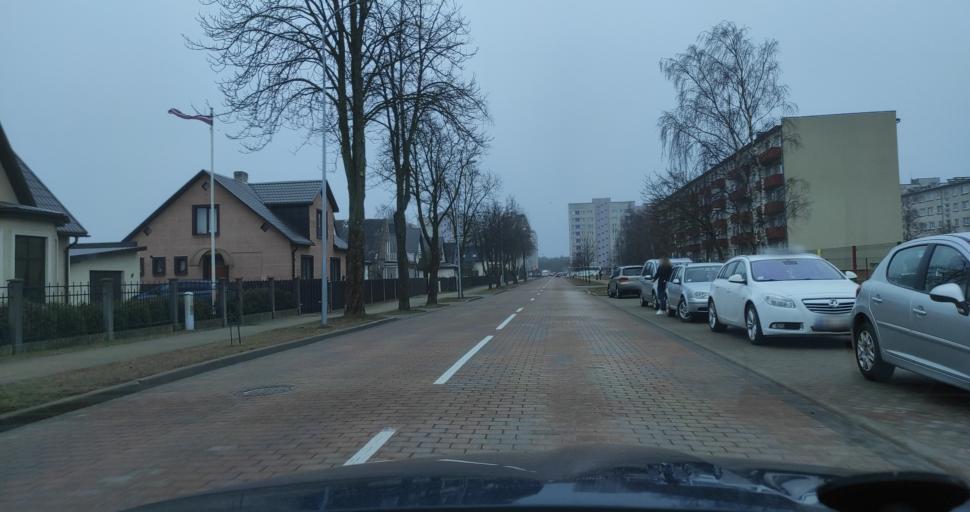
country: LV
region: Ventspils
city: Ventspils
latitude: 57.3863
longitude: 21.5519
